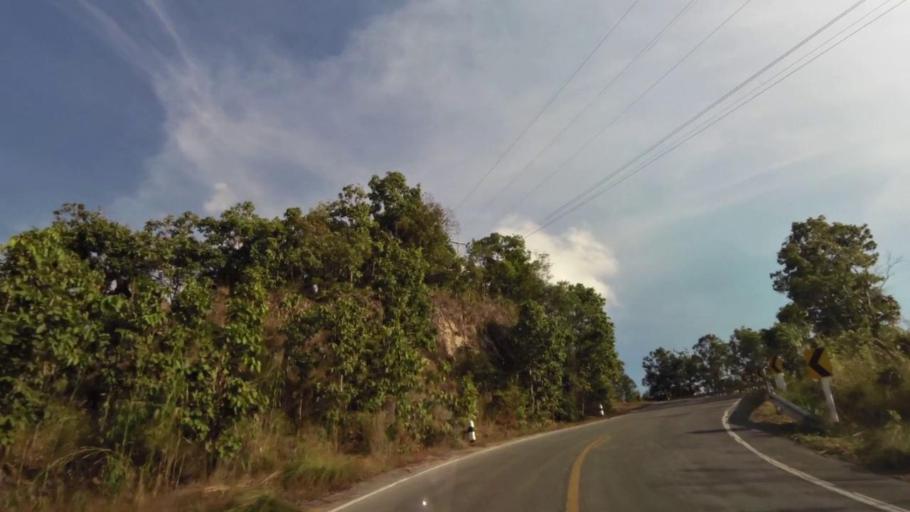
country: TH
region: Chiang Rai
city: Khun Tan
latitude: 19.8782
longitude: 100.3123
